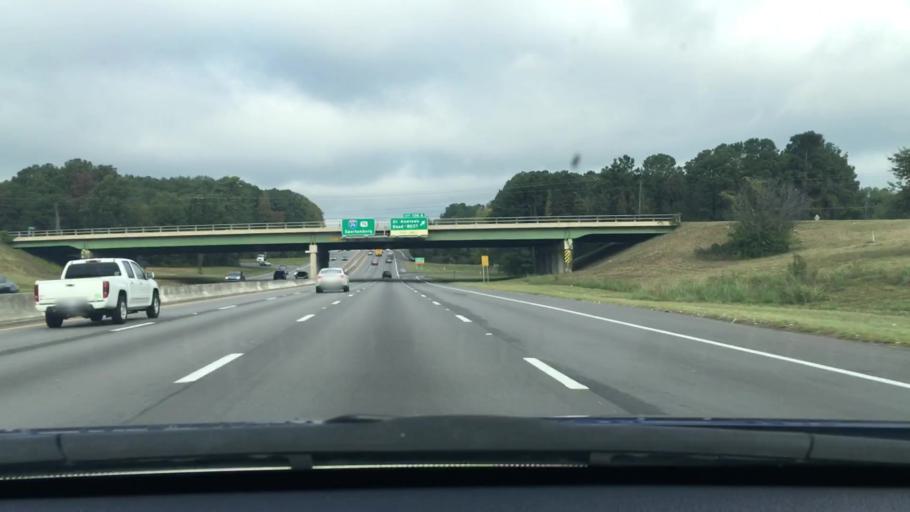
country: US
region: South Carolina
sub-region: Lexington County
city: Saint Andrews
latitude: 34.0438
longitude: -81.1170
